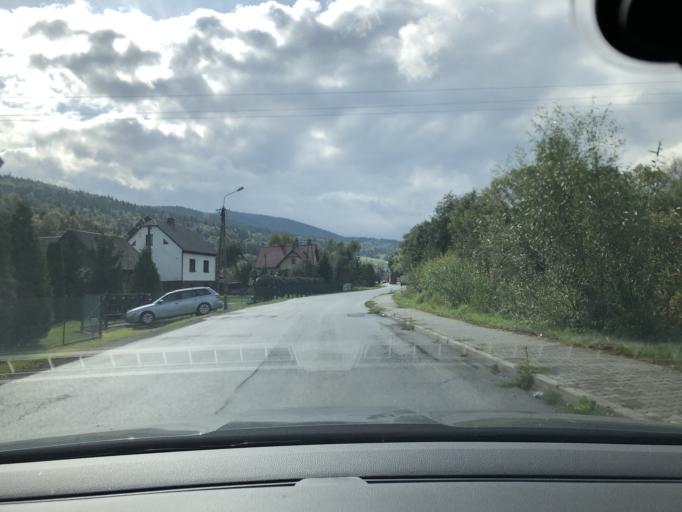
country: PL
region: Lesser Poland Voivodeship
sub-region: Powiat suski
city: Stryszawa
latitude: 49.7273
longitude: 19.5058
